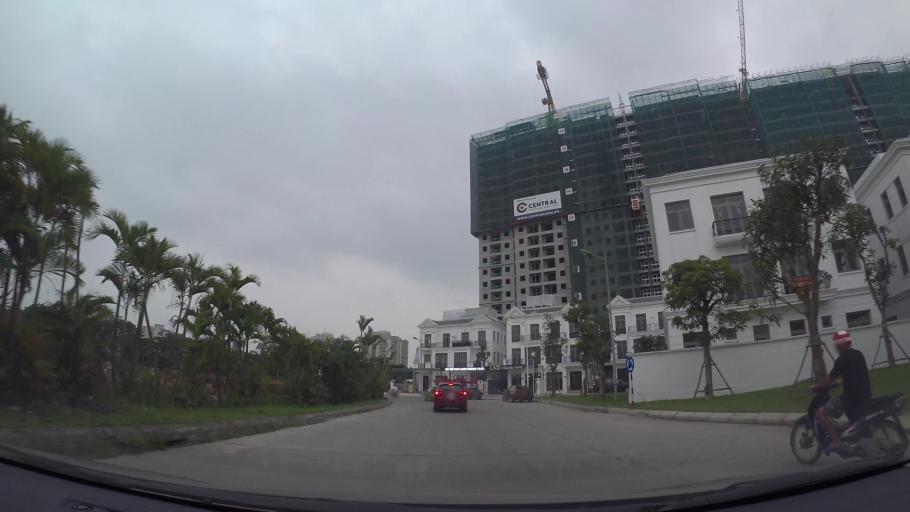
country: VN
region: Ha Noi
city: Trau Quy
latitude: 21.0430
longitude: 105.9055
